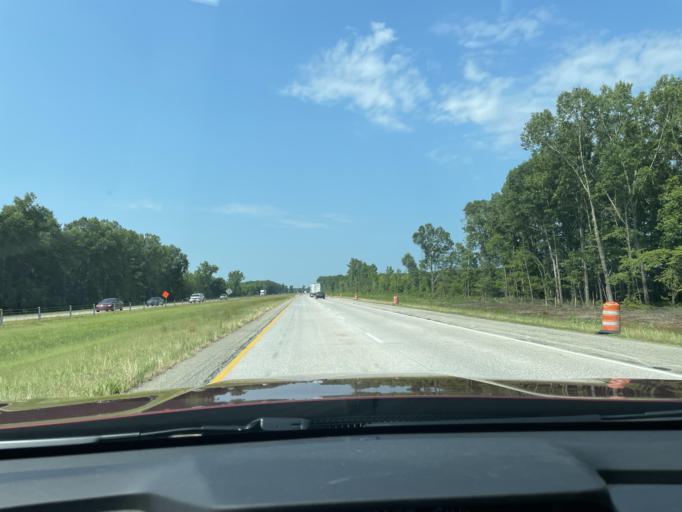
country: US
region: Arkansas
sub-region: White County
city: Searcy
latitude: 35.1584
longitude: -91.7838
